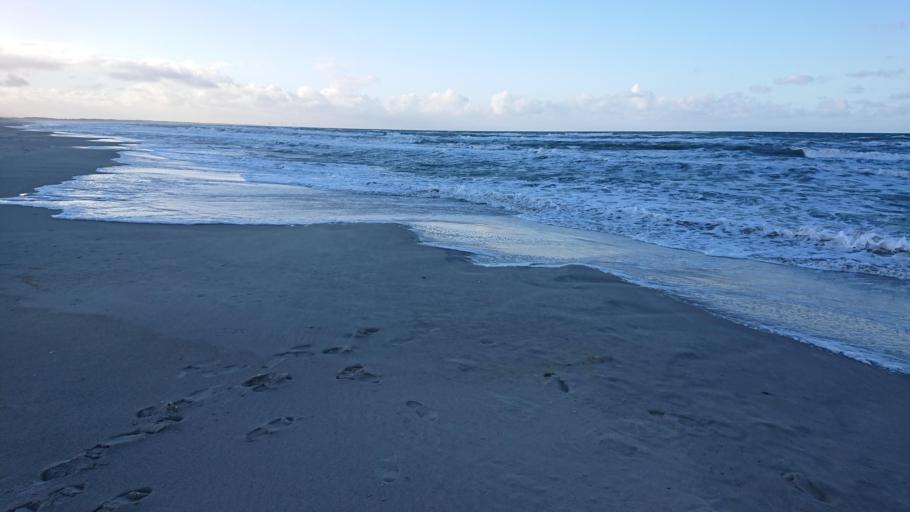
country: DK
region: North Denmark
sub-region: Hjorring Kommune
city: Sindal
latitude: 57.6092
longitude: 10.2308
